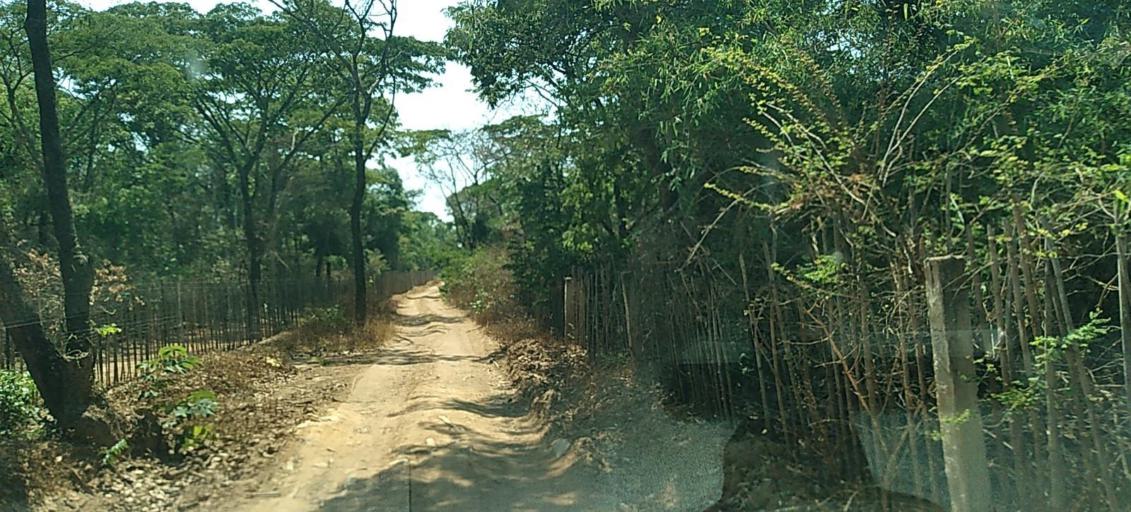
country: ZM
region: Copperbelt
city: Luanshya
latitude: -13.0089
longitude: 28.4580
